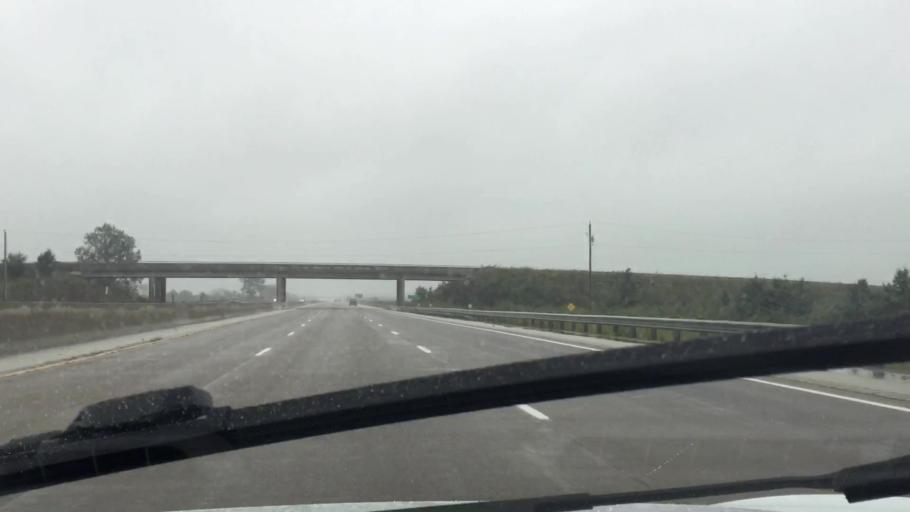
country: CA
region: Ontario
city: Windsor
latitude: 42.2422
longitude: -82.9321
